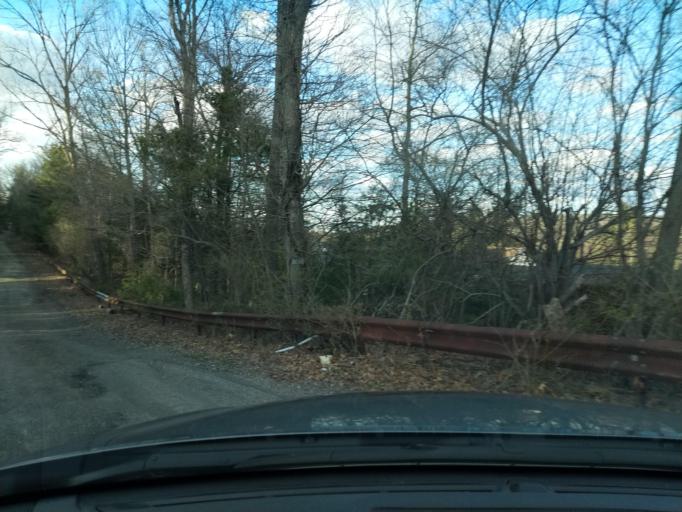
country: US
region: Connecticut
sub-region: Fairfield County
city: Newtown
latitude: 41.3680
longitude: -73.2731
